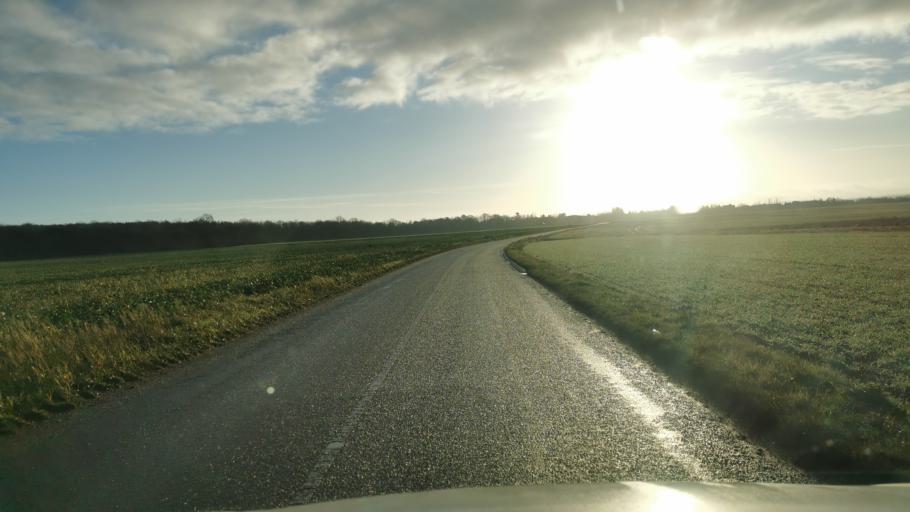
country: FR
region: Ile-de-France
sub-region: Departement des Yvelines
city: Houdan
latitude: 48.8318
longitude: 1.6238
